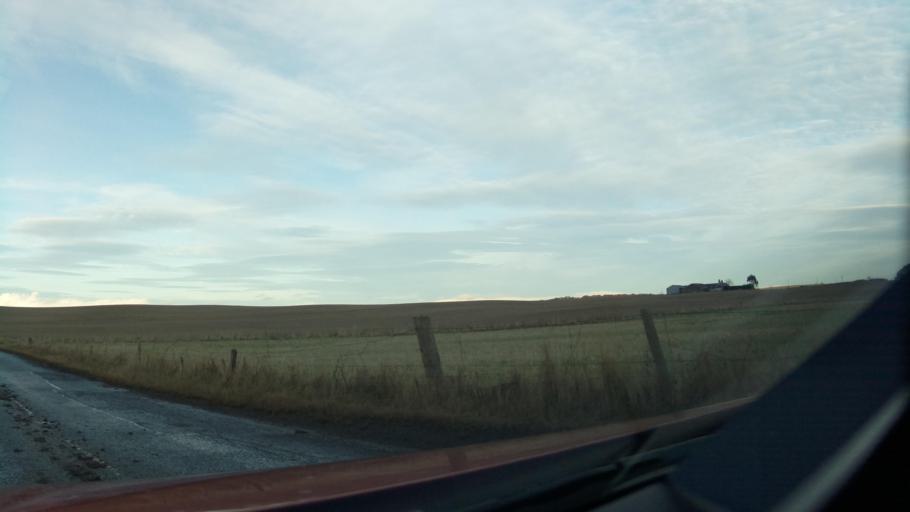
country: GB
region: Scotland
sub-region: Angus
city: Letham
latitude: 56.5694
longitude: -2.7779
